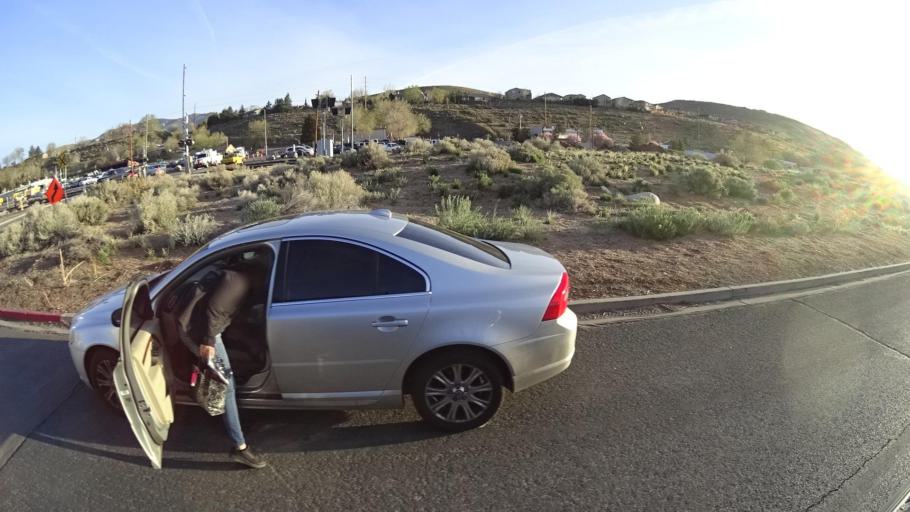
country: US
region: Nevada
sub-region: Washoe County
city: Mogul
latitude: 39.5075
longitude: -119.8959
